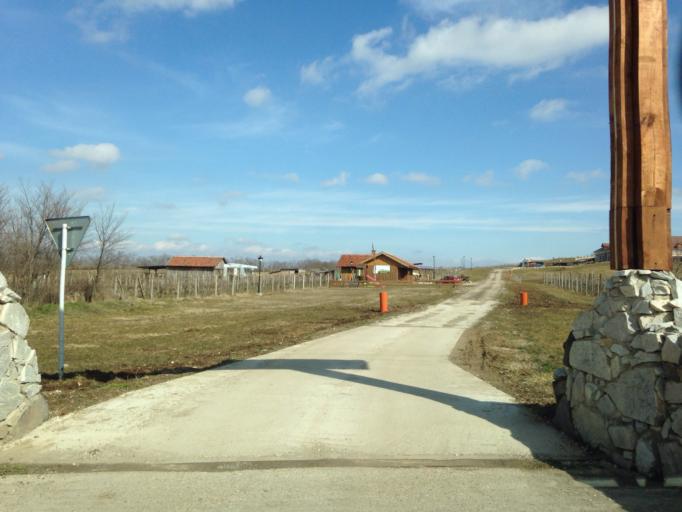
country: SK
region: Nitriansky
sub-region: Okres Komarno
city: Hurbanovo
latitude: 47.8462
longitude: 18.2752
